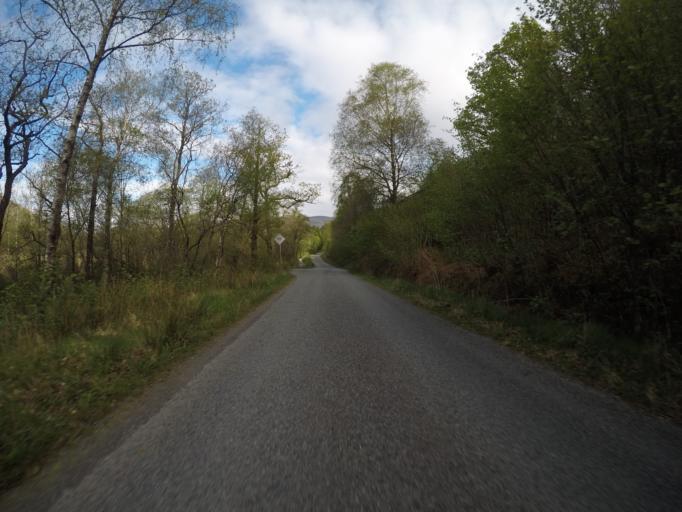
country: GB
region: Scotland
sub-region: Highland
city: Fort William
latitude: 56.6778
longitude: -5.0812
